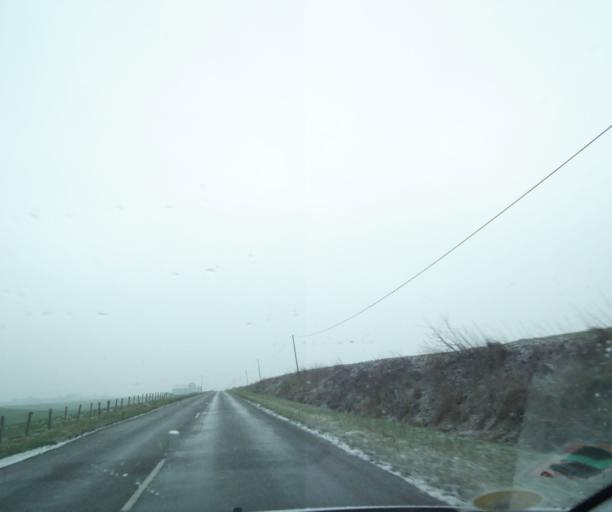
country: FR
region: Champagne-Ardenne
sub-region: Departement de la Haute-Marne
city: Wassy
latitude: 48.4880
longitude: 4.9759
